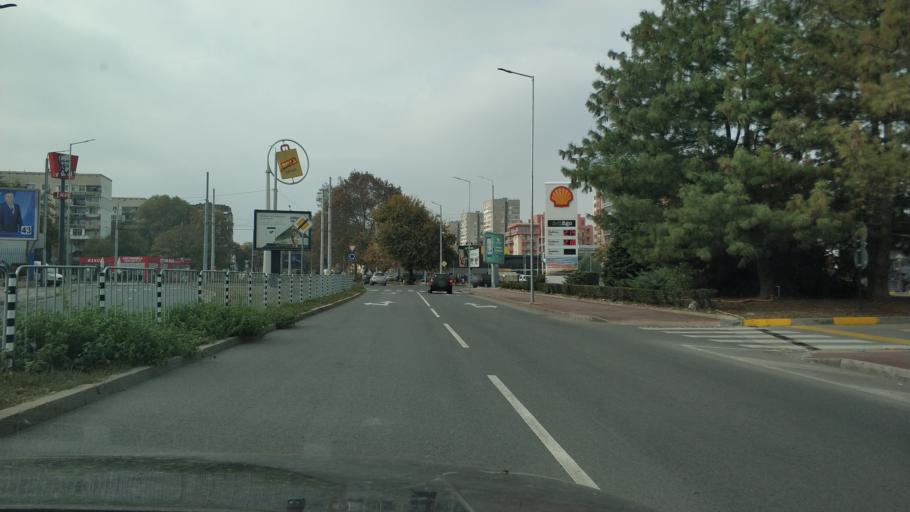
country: BG
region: Plovdiv
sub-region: Obshtina Plovdiv
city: Plovdiv
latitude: 42.1530
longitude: 24.7643
